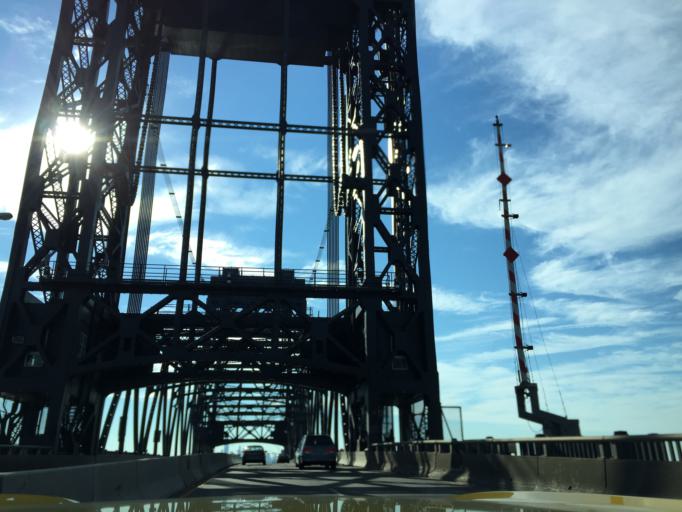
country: US
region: New Jersey
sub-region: Hudson County
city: Harrison
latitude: 40.7327
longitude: -74.1191
